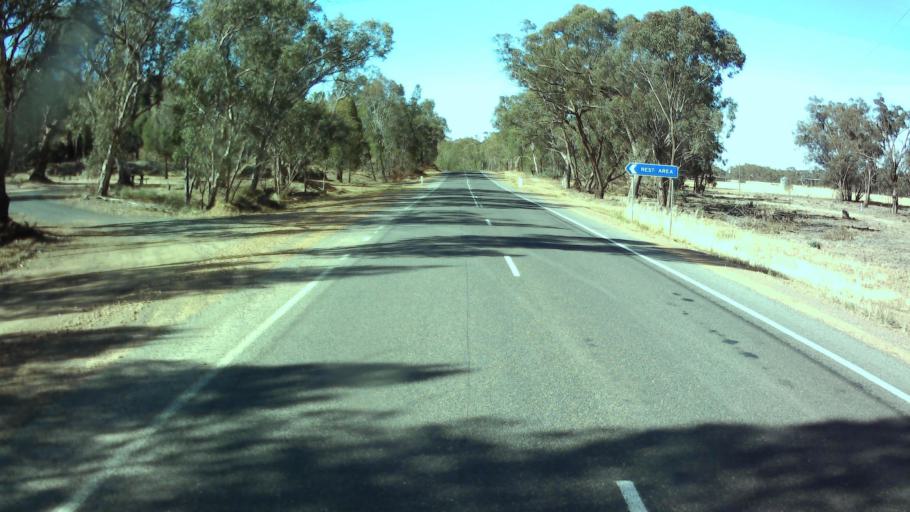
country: AU
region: New South Wales
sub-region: Weddin
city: Grenfell
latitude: -33.7478
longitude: 148.0868
